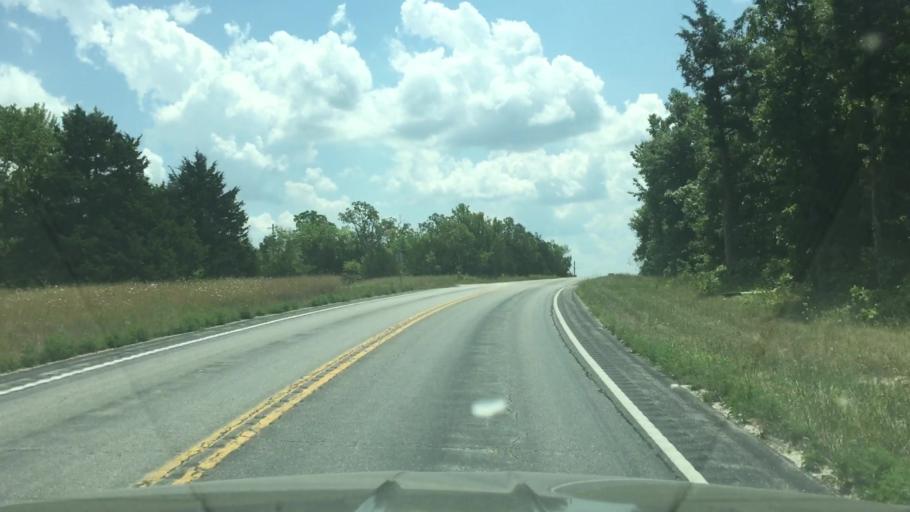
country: US
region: Missouri
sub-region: Miller County
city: Tuscumbia
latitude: 38.1154
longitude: -92.5087
